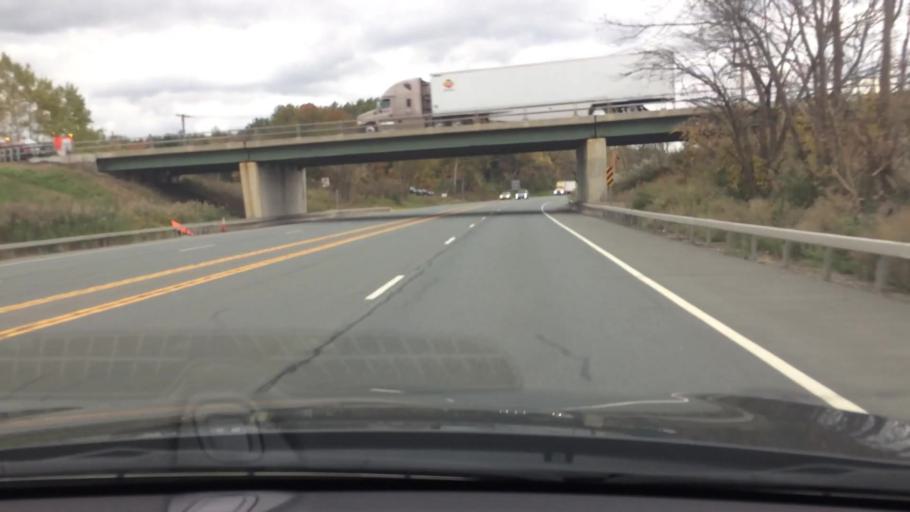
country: US
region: New York
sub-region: Columbia County
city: Niverville
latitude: 42.4825
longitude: -73.6800
